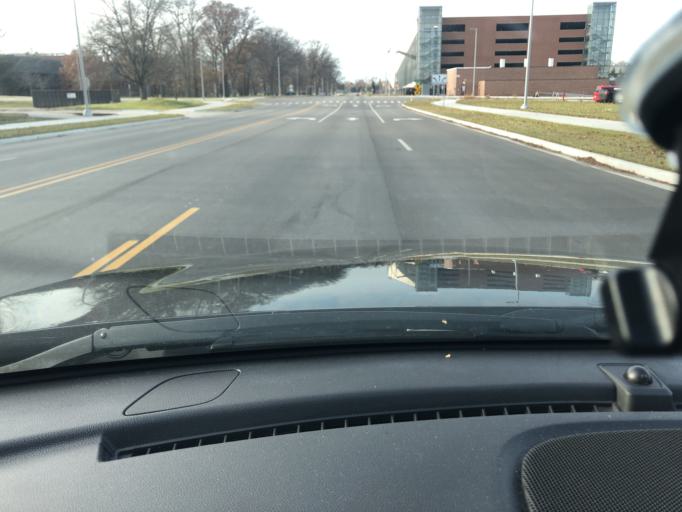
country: US
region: Michigan
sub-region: Wayne County
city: Allen Park
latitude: 42.2932
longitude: -83.2334
